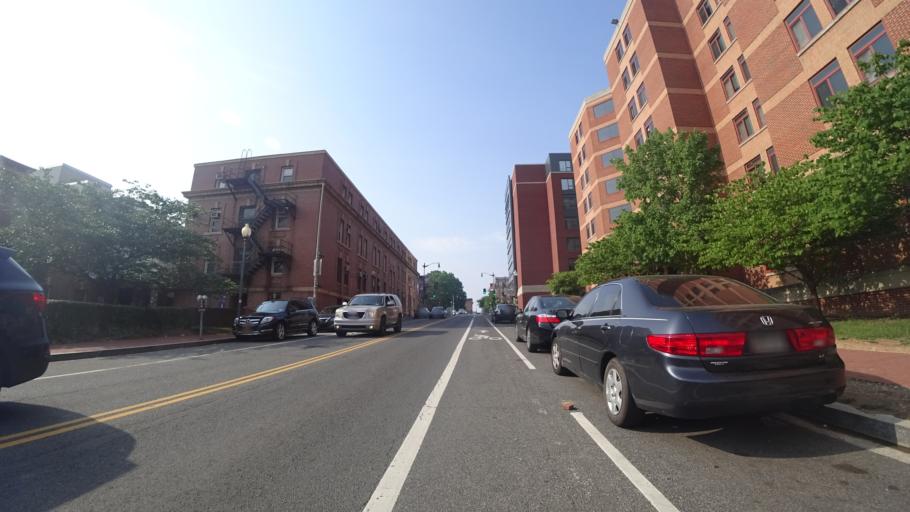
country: US
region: Washington, D.C.
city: Washington, D.C.
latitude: 38.9207
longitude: -77.0180
